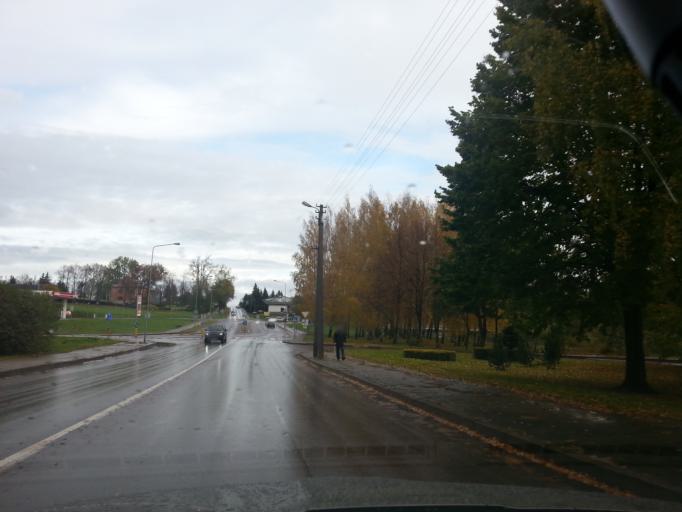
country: LT
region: Marijampoles apskritis
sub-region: Marijampole Municipality
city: Marijampole
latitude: 54.5666
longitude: 23.3401
